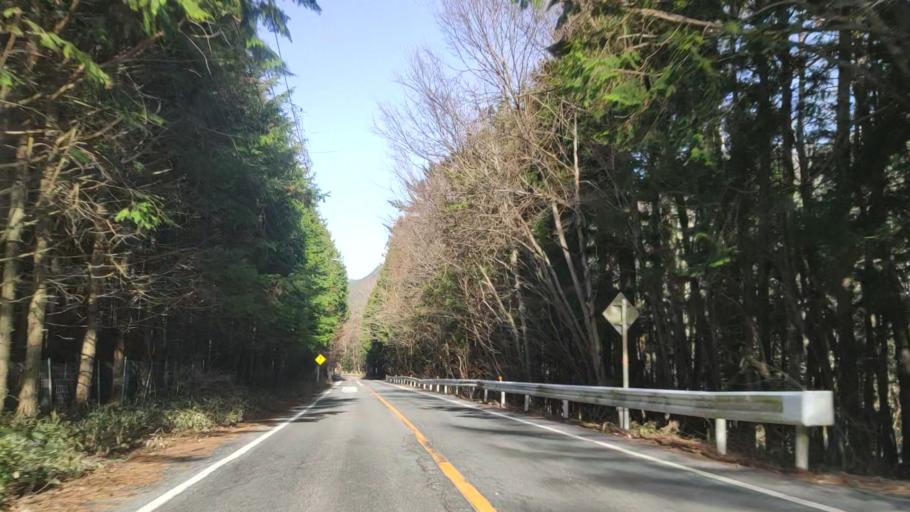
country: JP
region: Yamanashi
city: Fujikawaguchiko
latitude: 35.5511
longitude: 138.6933
